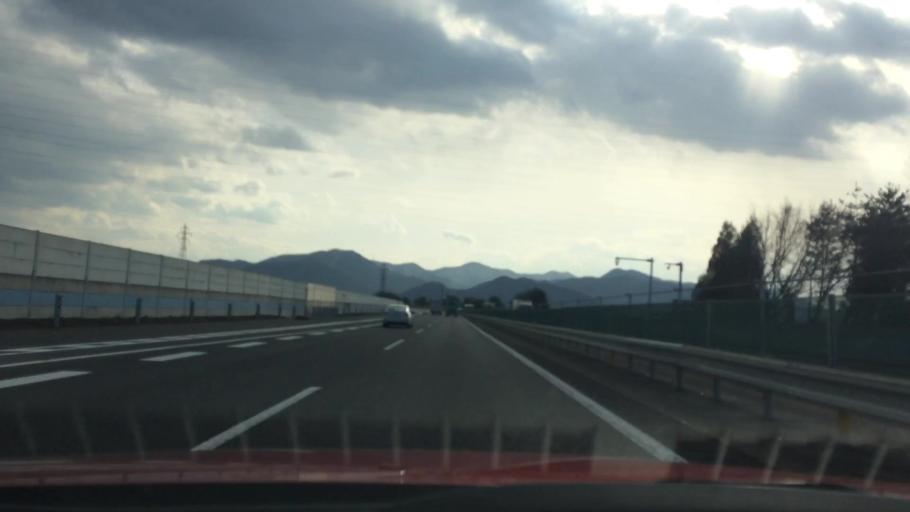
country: JP
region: Nagano
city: Shiojiri
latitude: 36.1434
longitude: 137.9673
